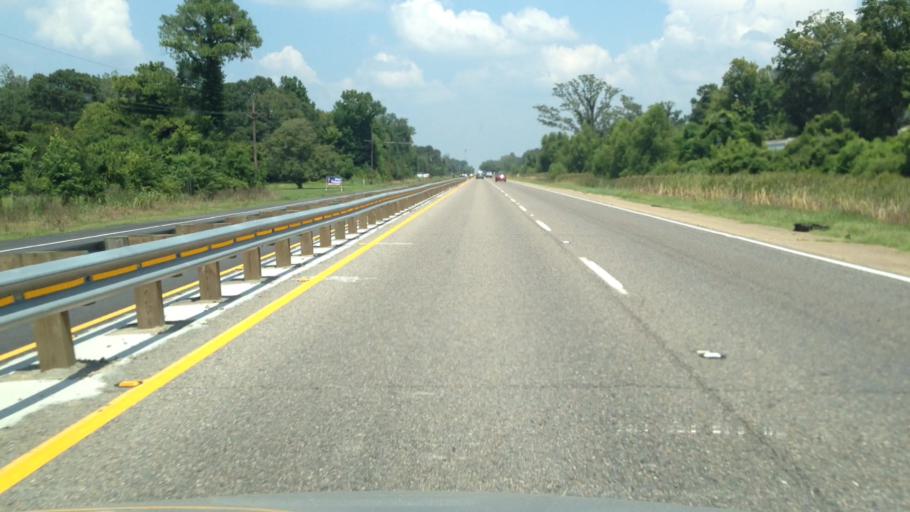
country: US
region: Louisiana
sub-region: Pointe Coupee Parish
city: Livonia
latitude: 30.5558
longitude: -91.6065
